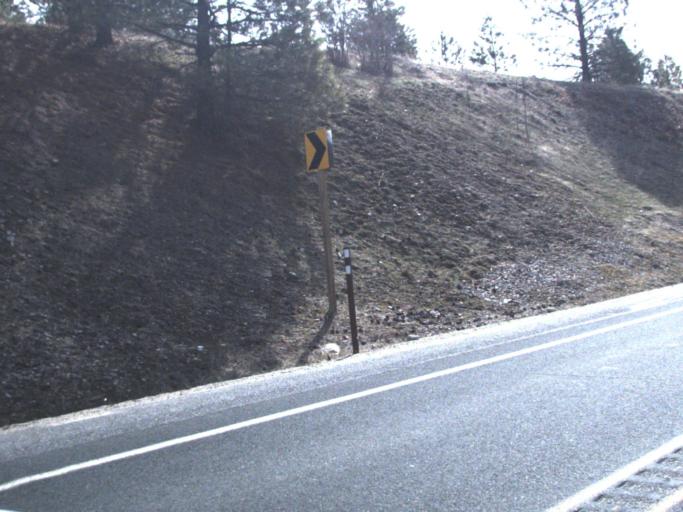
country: US
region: Washington
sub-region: Stevens County
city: Colville
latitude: 48.5132
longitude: -117.7300
